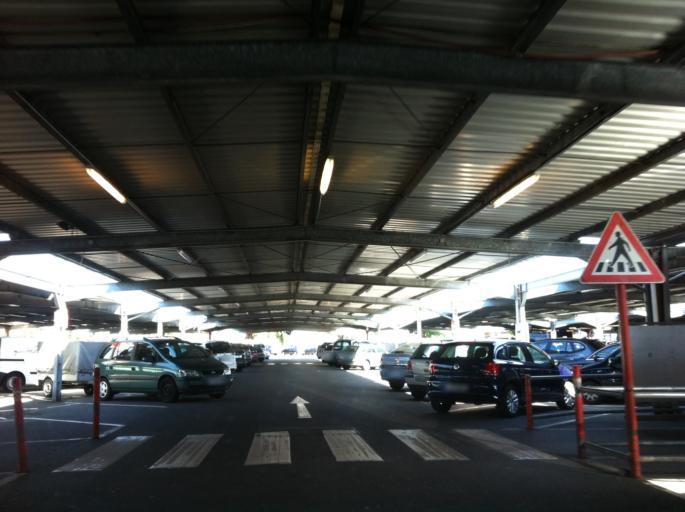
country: DE
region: Hesse
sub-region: Regierungsbezirk Darmstadt
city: Eschborn
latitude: 50.1350
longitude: 8.6009
